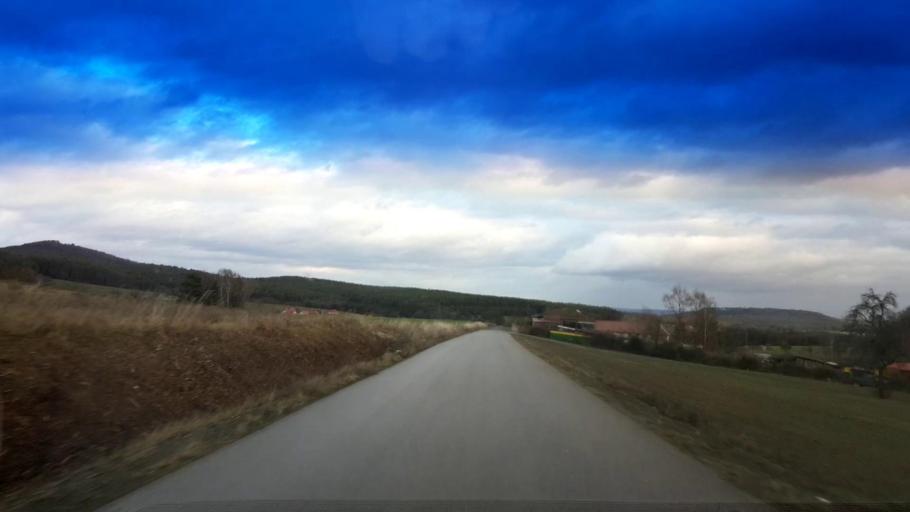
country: DE
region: Bavaria
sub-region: Upper Franconia
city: Lauter
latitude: 49.9800
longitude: 10.7620
